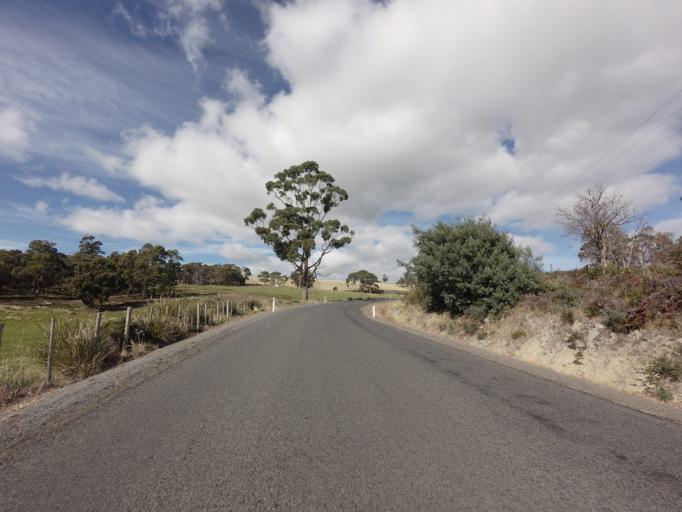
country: AU
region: Tasmania
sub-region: Clarence
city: Sandford
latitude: -43.0368
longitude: 147.7324
